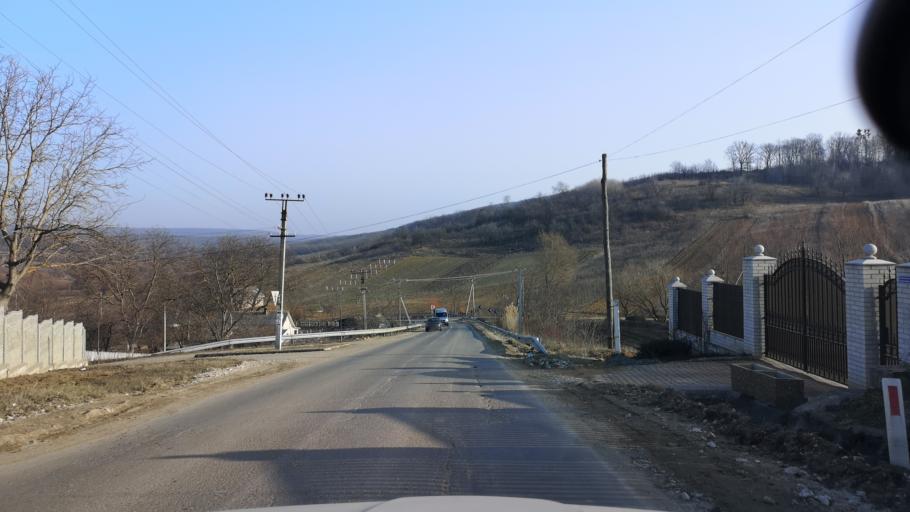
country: MD
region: Stinga Nistrului
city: Bucovat
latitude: 47.1086
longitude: 28.5042
